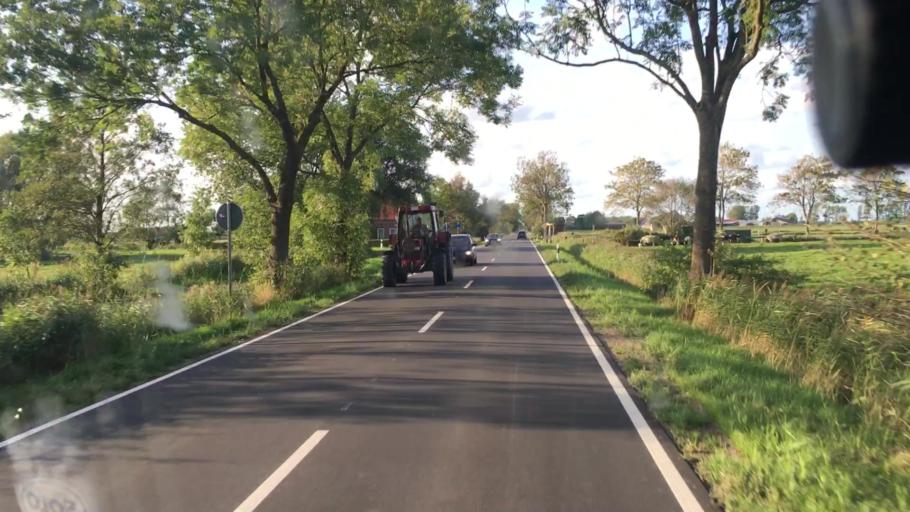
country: DE
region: Lower Saxony
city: Jever
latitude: 53.6149
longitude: 7.8669
